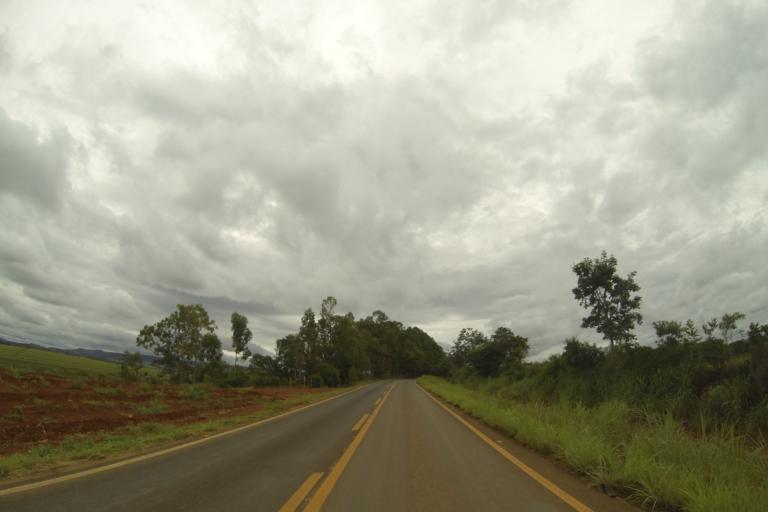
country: BR
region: Minas Gerais
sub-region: Bambui
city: Bambui
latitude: -20.0191
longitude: -46.1963
